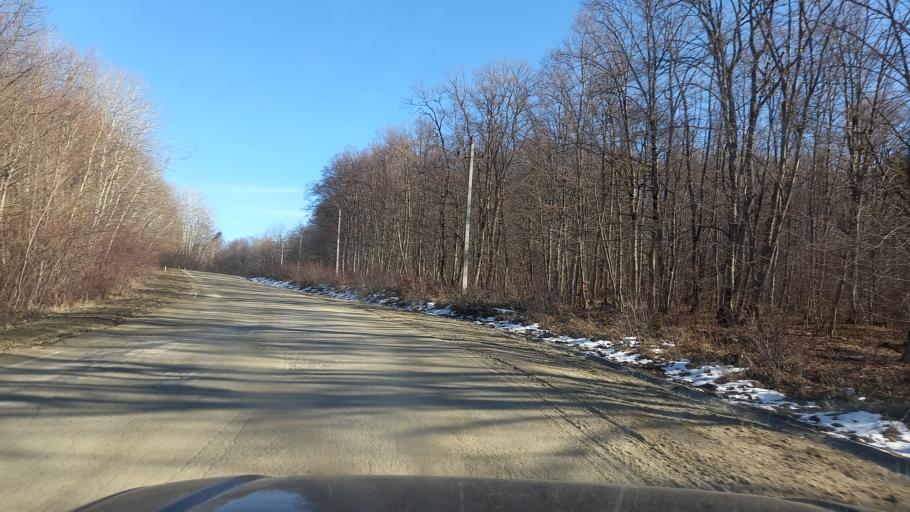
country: RU
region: Adygeya
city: Kamennomostskiy
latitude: 44.2744
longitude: 40.2787
